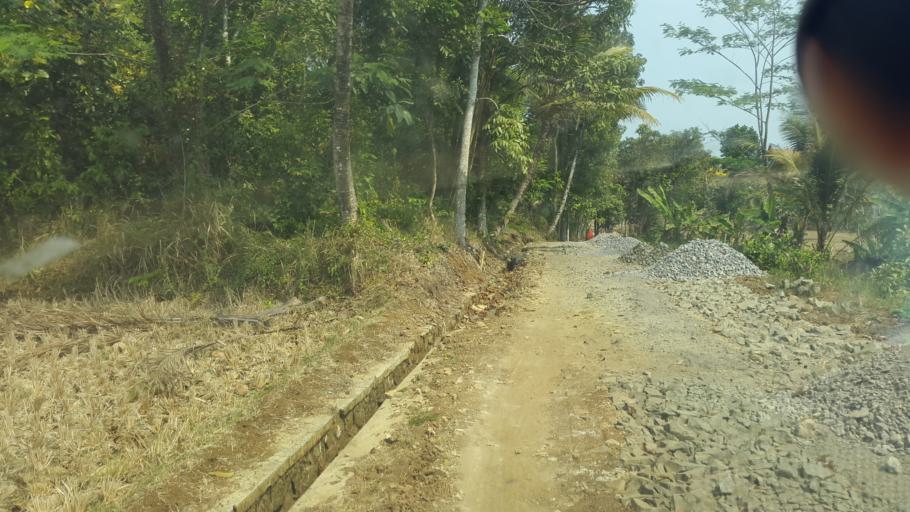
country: ID
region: West Java
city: Leuwinanggung Satu
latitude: -7.3095
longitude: 106.6347
